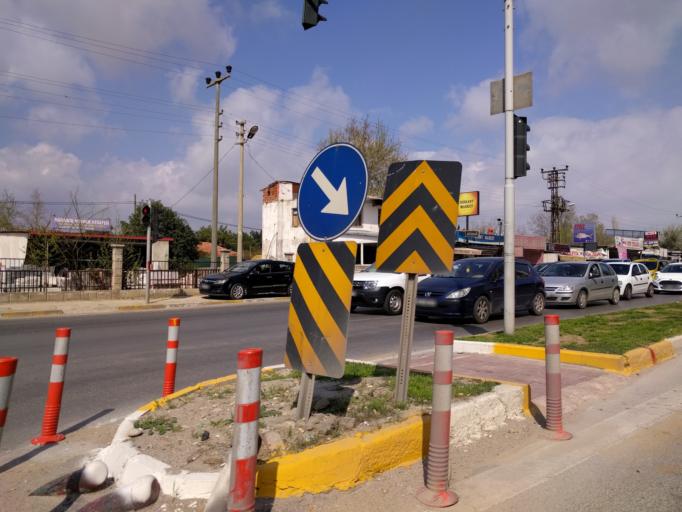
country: TR
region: Antalya
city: Antalya
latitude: 36.8999
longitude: 30.6308
